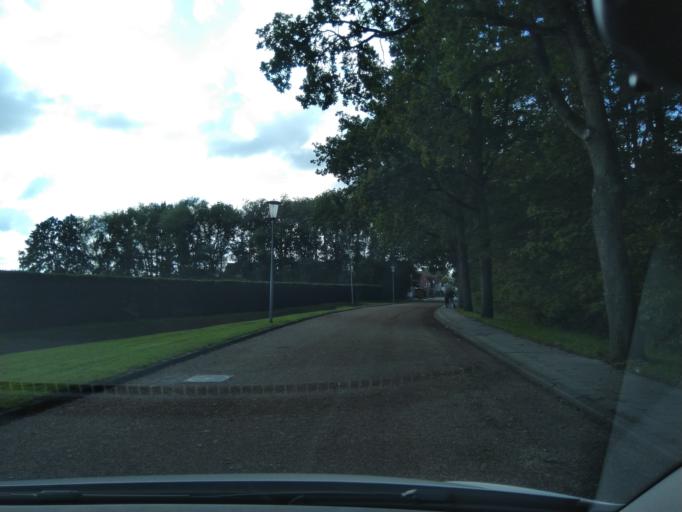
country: NL
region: Groningen
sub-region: Gemeente Veendam
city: Veendam
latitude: 53.0923
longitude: 6.9070
